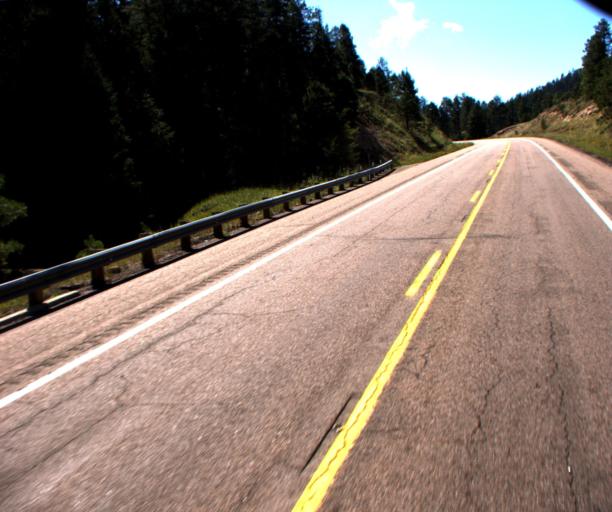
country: US
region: Arizona
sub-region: Apache County
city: Eagar
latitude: 33.9066
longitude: -109.1657
